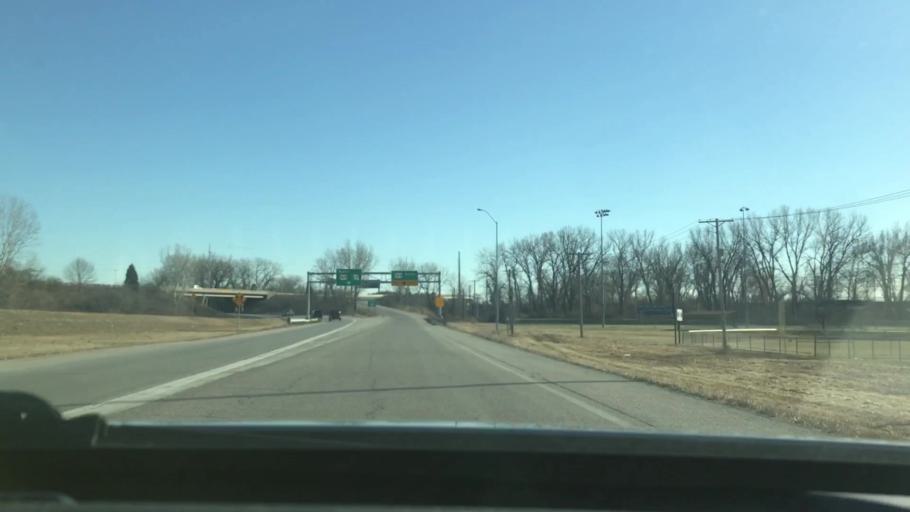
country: US
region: Missouri
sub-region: Platte County
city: Riverside
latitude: 39.1606
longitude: -94.5913
